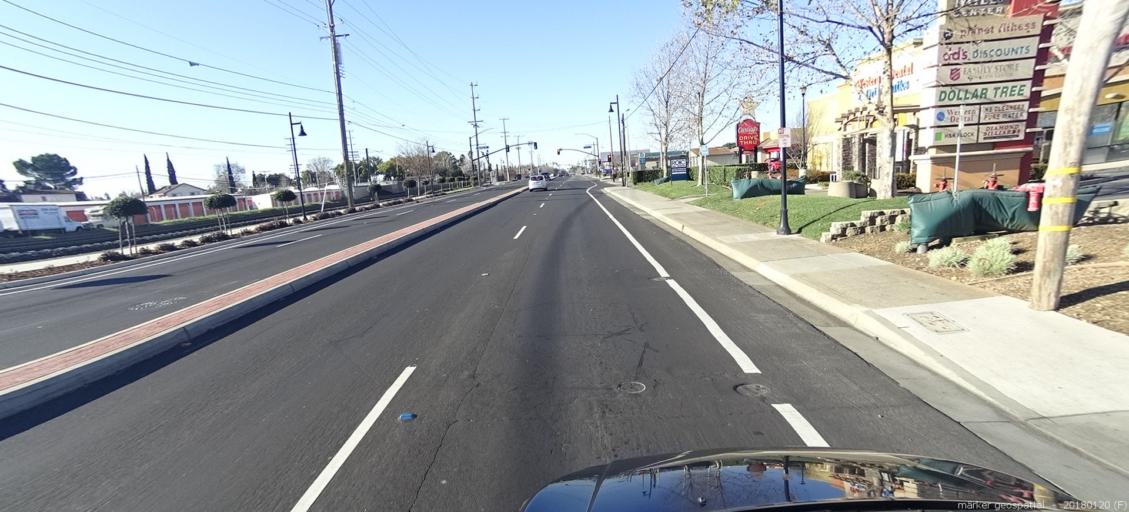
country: US
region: California
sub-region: Sacramento County
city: Rancho Cordova
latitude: 38.5873
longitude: -121.3068
